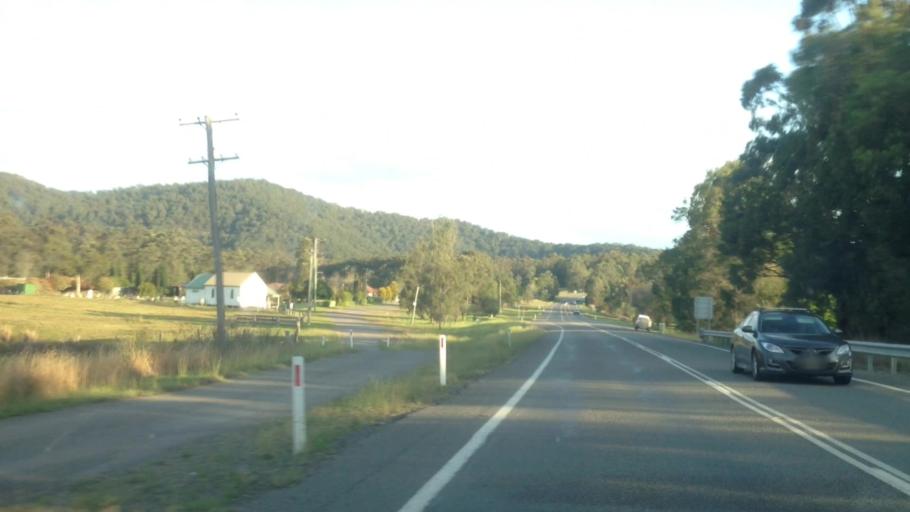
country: AU
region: New South Wales
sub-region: Lake Macquarie Shire
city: Holmesville
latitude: -32.9505
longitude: 151.4793
